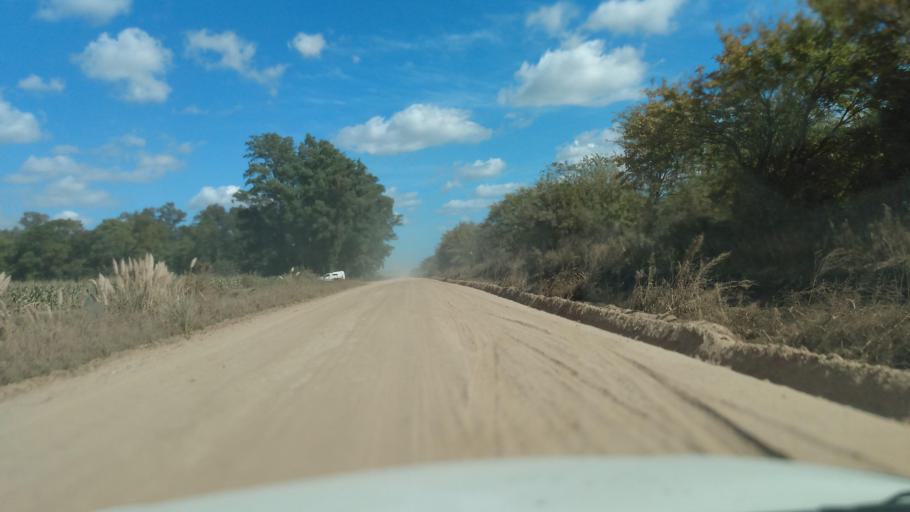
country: AR
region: Buenos Aires
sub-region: Partido de Navarro
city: Navarro
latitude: -35.0238
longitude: -59.4367
